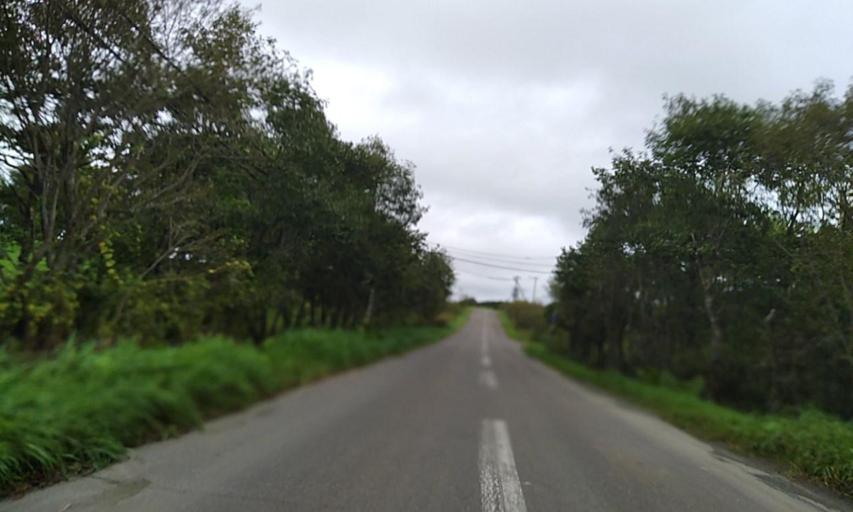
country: JP
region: Hokkaido
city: Nemuro
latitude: 43.2623
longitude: 145.2625
